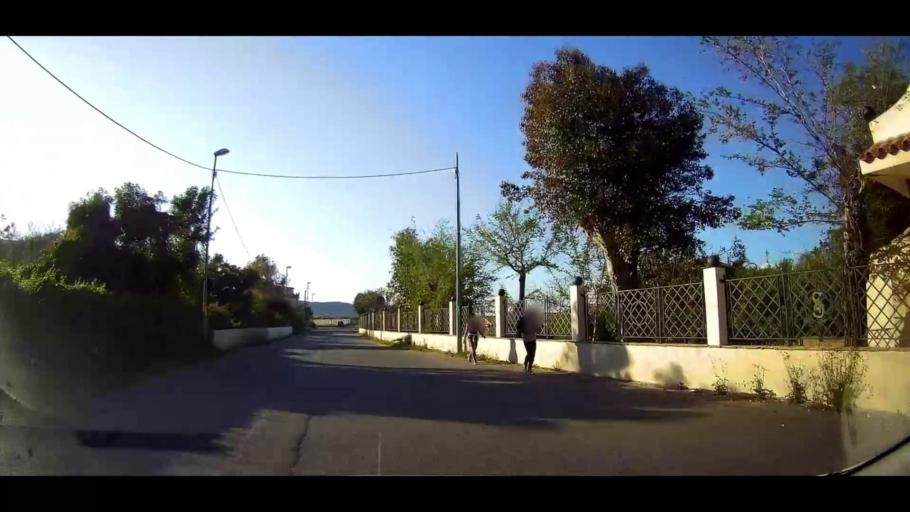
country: IT
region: Calabria
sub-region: Provincia di Crotone
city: Crotone
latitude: 39.0485
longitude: 17.1444
